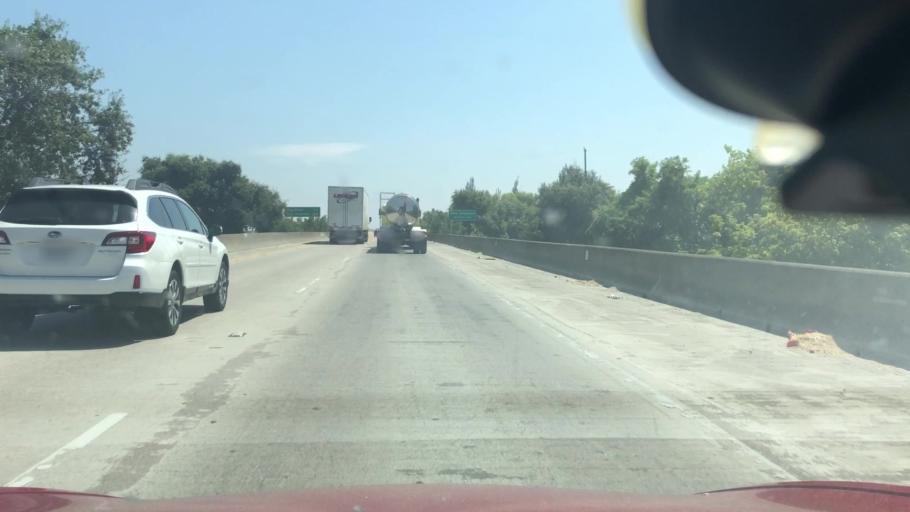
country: US
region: California
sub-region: San Joaquin County
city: Thornton
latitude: 38.2554
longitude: -121.4483
